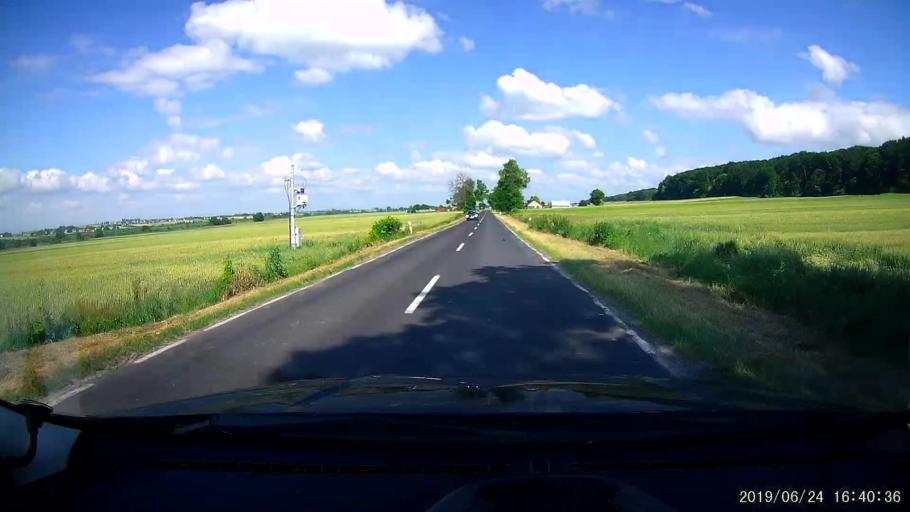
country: PL
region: Lublin Voivodeship
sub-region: Powiat tomaszowski
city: Rachanie
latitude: 50.5305
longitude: 23.5766
